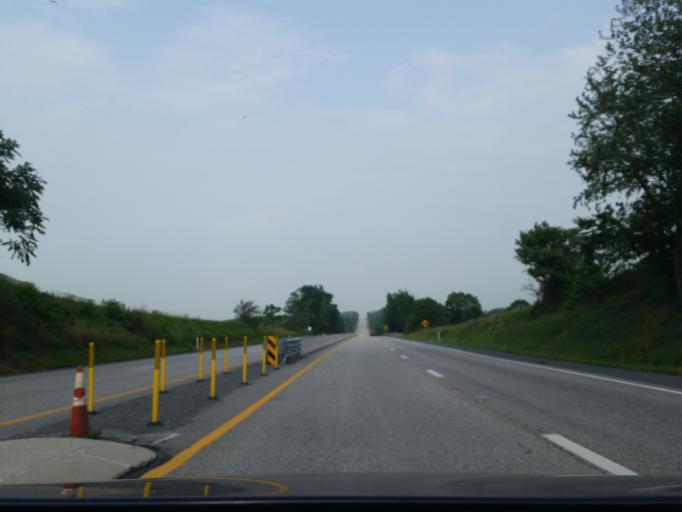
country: US
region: Pennsylvania
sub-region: Lebanon County
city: Jonestown
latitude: 40.4073
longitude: -76.5620
